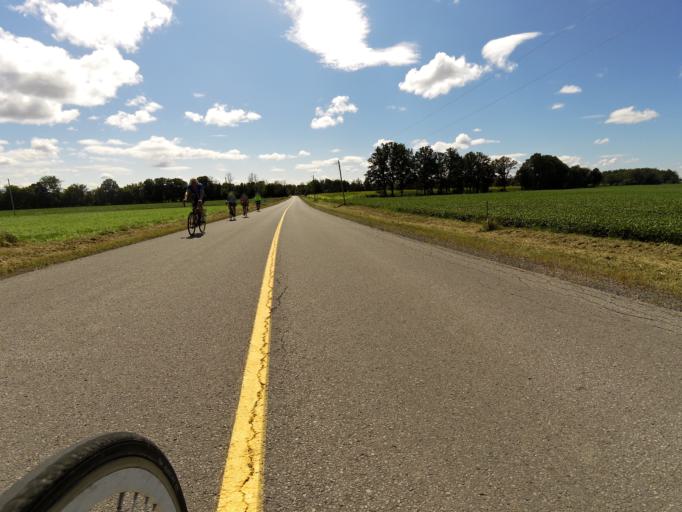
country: CA
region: Ontario
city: Bells Corners
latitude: 45.2595
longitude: -75.8093
